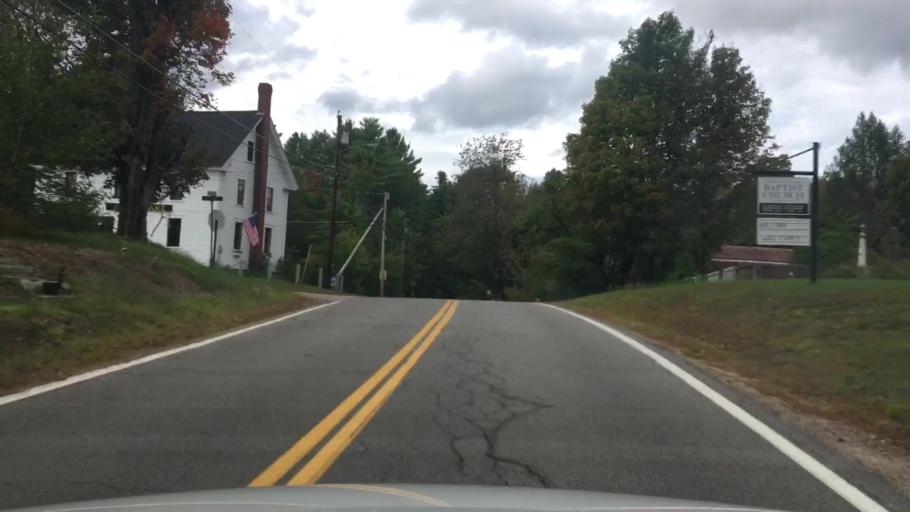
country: US
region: New Hampshire
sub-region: Carroll County
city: Effingham
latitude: 43.7390
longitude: -71.0090
